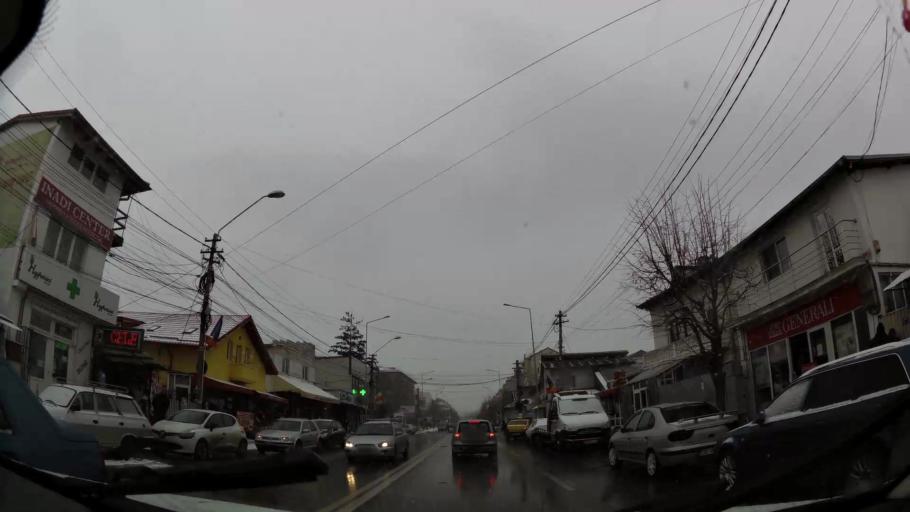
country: RO
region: Dambovita
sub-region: Municipiul Targoviste
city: Targoviste
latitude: 44.9233
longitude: 25.4519
